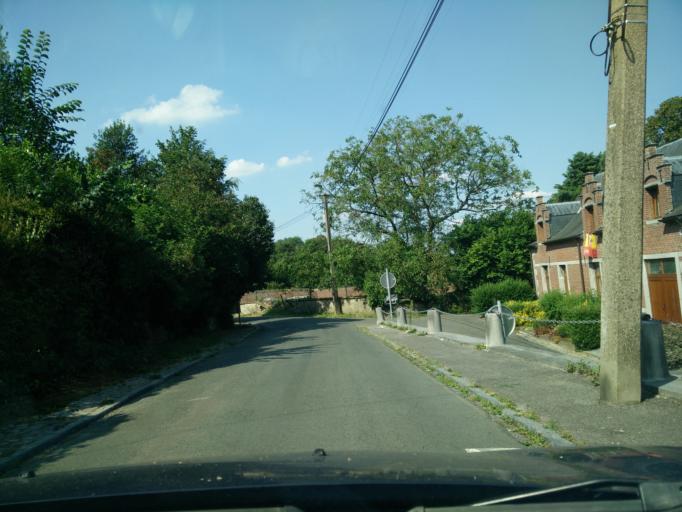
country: BE
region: Wallonia
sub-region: Province du Hainaut
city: Ecaussinnes-d'Enghien
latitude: 50.5725
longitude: 4.1776
